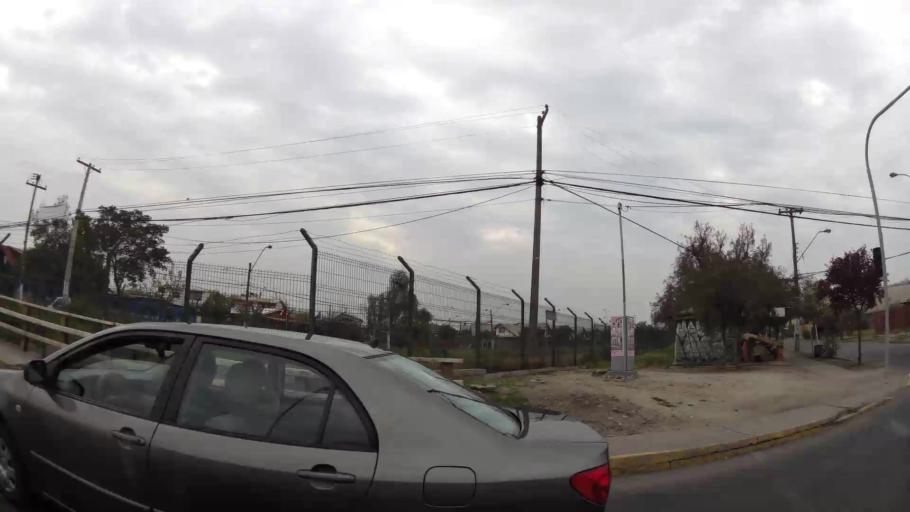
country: CL
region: Santiago Metropolitan
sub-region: Provincia de Santiago
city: Villa Presidente Frei, Nunoa, Santiago, Chile
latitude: -33.4995
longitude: -70.6025
